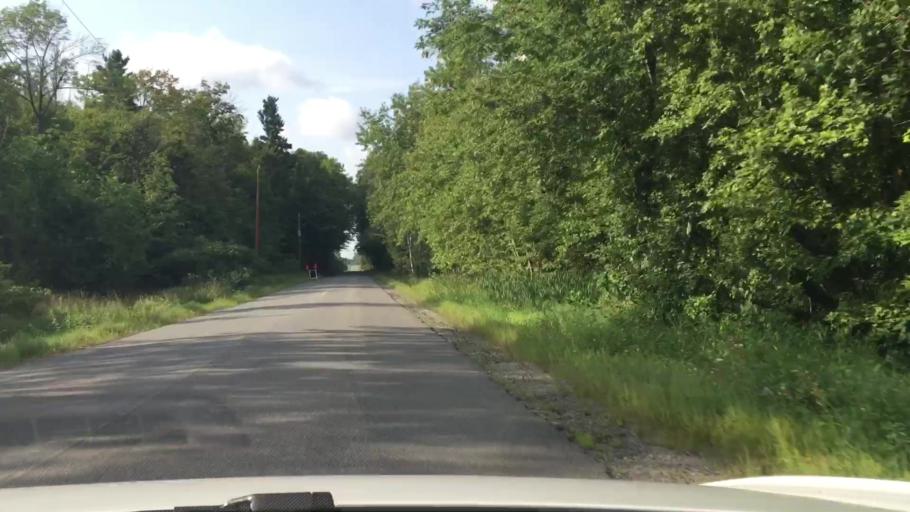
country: CA
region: Ontario
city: Oshawa
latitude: 43.9446
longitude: -78.7497
